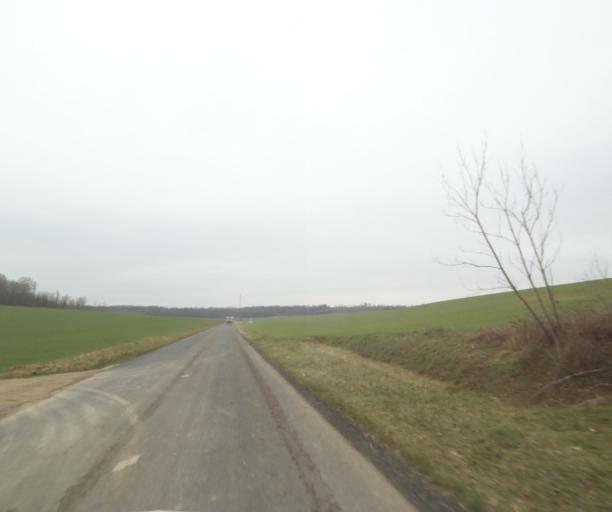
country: FR
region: Champagne-Ardenne
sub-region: Departement de la Haute-Marne
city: Bienville
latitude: 48.5787
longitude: 5.0324
